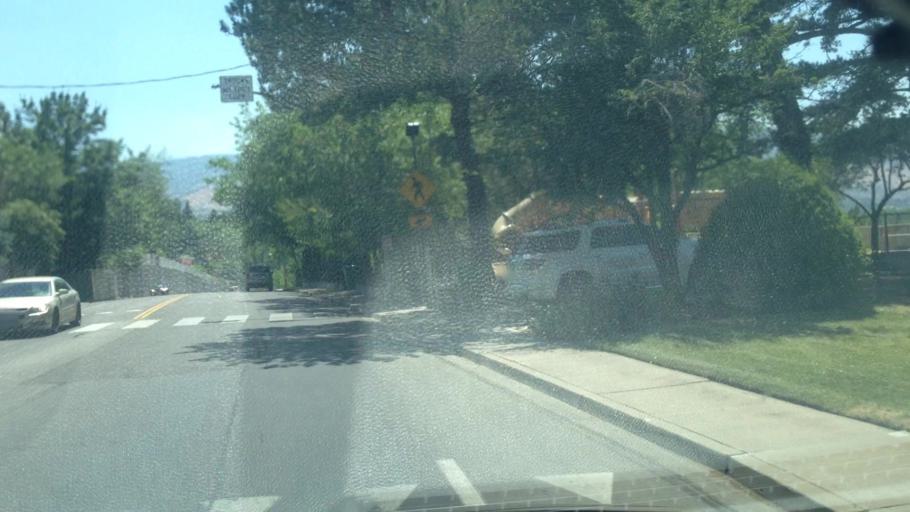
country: US
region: Nevada
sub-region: Washoe County
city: Reno
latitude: 39.5183
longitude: -119.8240
